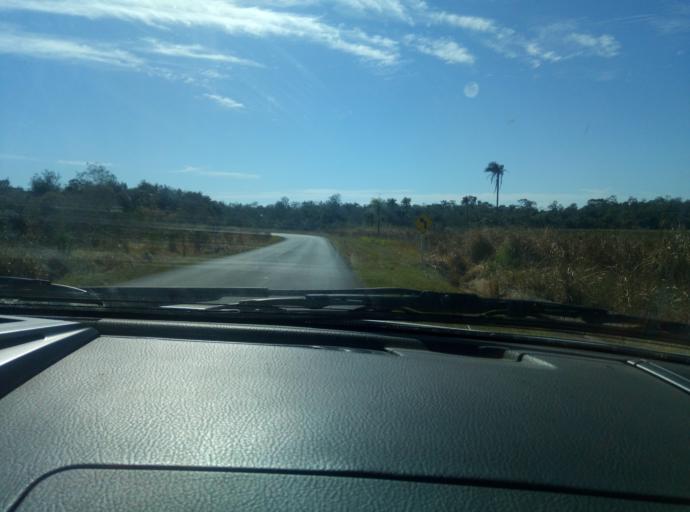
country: PY
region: Caaguazu
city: Carayao
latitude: -25.1812
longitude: -56.3123
